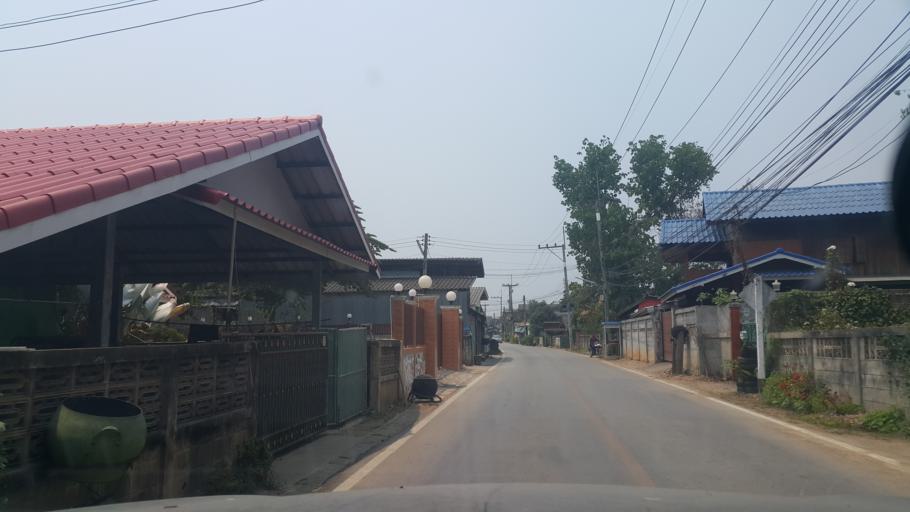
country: TH
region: Lampang
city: Soem Ngam
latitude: 18.0731
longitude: 99.2318
